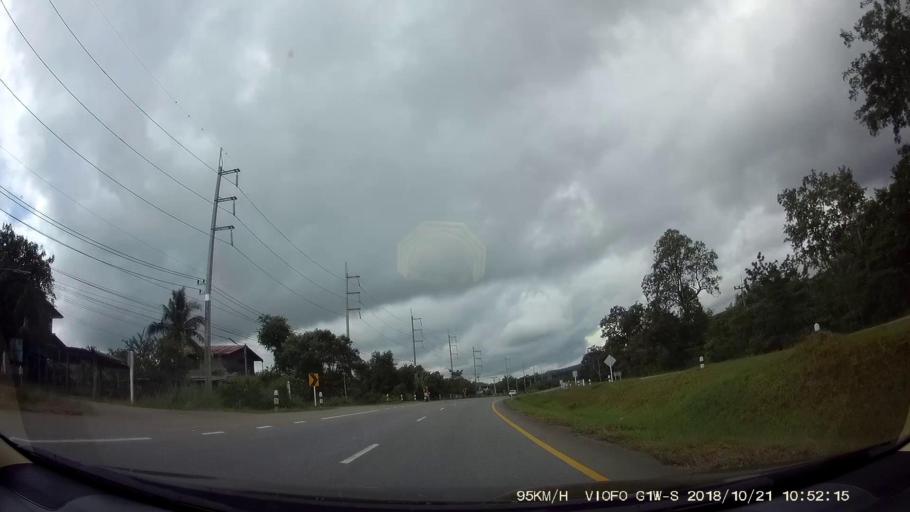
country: TH
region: Chaiyaphum
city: Khon Sawan
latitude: 15.9779
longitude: 102.1956
